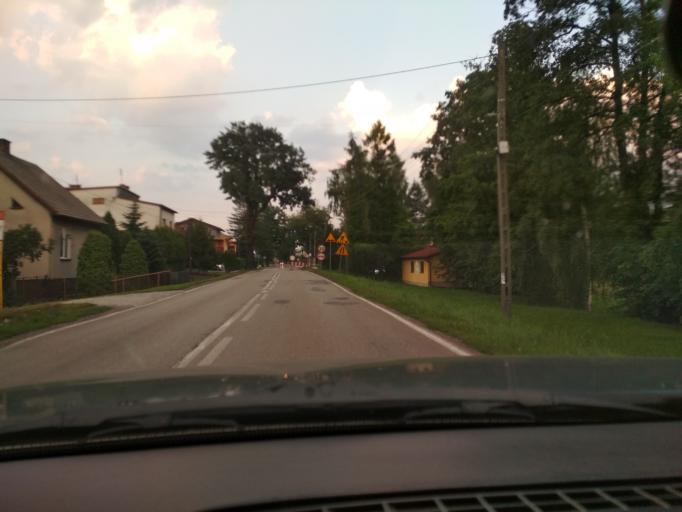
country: PL
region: Silesian Voivodeship
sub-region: Powiat cieszynski
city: Mnich
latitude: 49.8977
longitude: 18.7962
